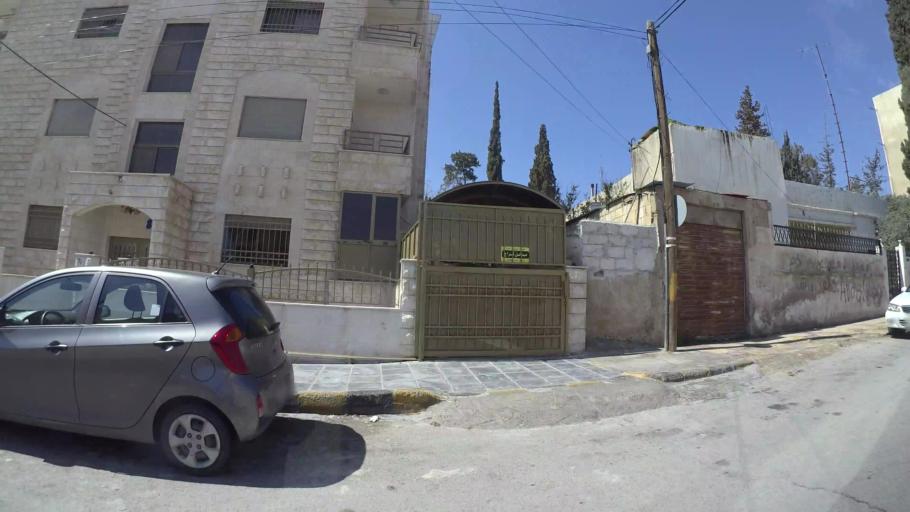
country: JO
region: Amman
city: Amman
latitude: 31.9813
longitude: 35.9915
